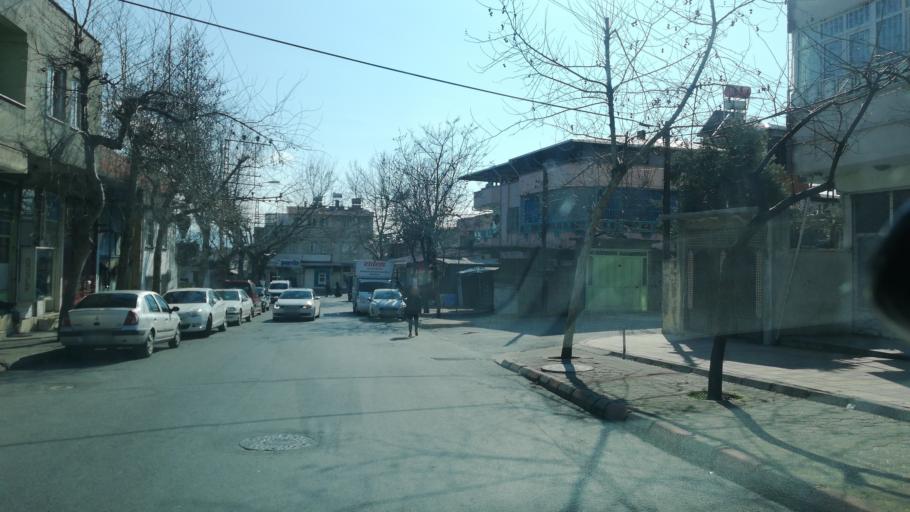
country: TR
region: Kahramanmaras
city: Kahramanmaras
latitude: 37.5721
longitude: 36.9473
